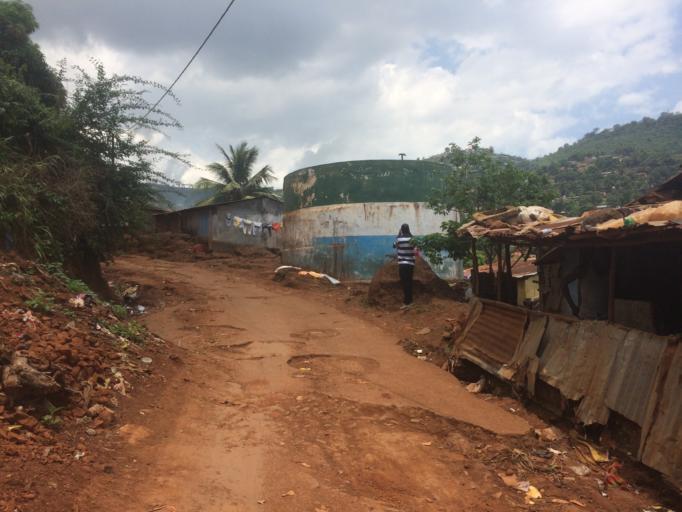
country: SL
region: Western Area
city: Freetown
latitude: 8.4739
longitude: -13.2054
